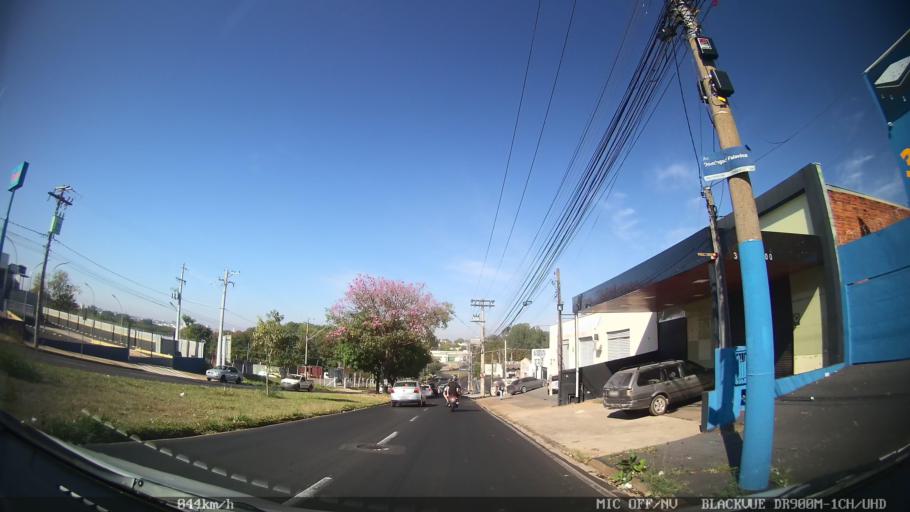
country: BR
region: Sao Paulo
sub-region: Sao Jose Do Rio Preto
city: Sao Jose do Rio Preto
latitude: -20.7770
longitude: -49.3857
